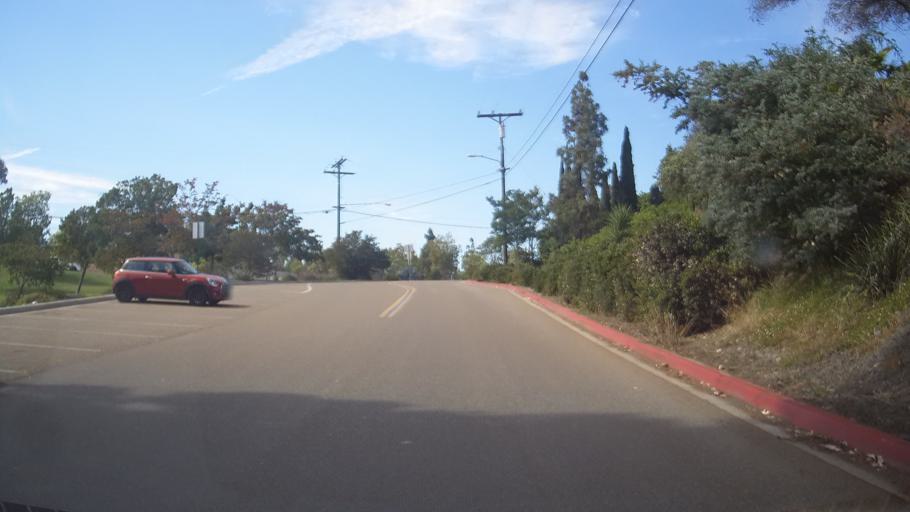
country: US
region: California
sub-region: San Diego County
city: La Mesa
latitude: 32.7904
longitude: -117.0050
